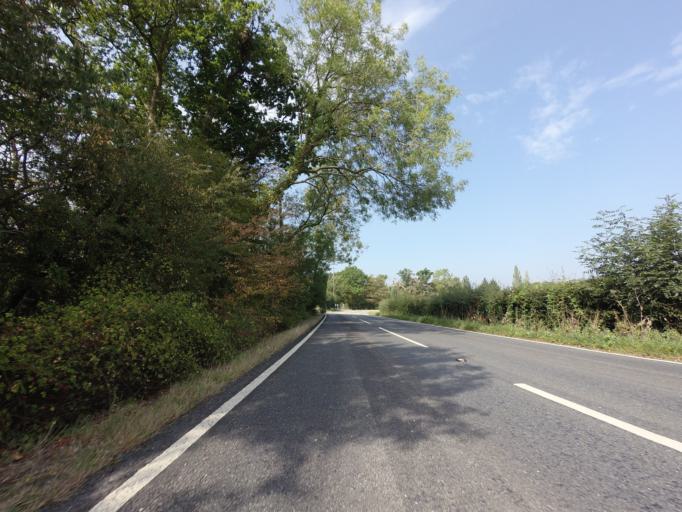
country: GB
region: England
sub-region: Kent
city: Headcorn
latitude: 51.1173
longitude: 0.6118
